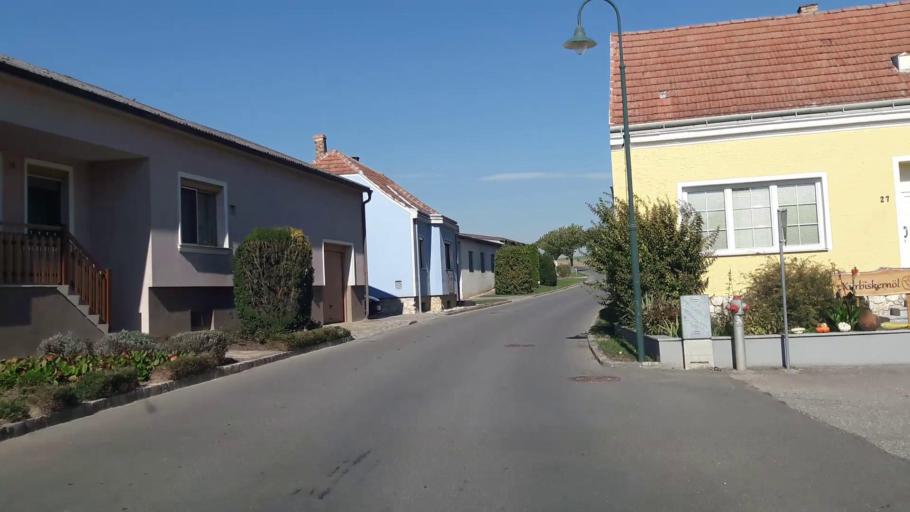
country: AT
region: Lower Austria
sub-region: Politischer Bezirk Korneuburg
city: Ernstbrunn
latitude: 48.4974
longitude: 16.3638
